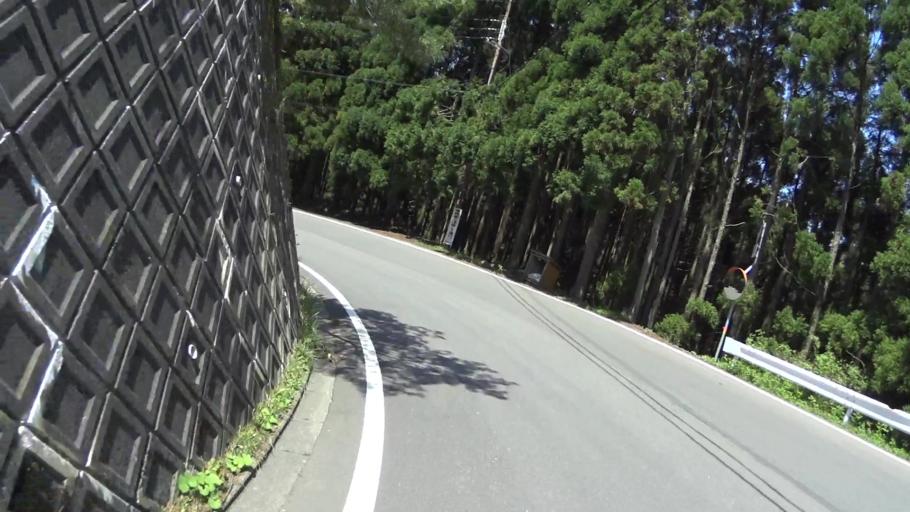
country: JP
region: Kyoto
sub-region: Kyoto-shi
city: Kamigyo-ku
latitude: 35.1611
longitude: 135.7818
